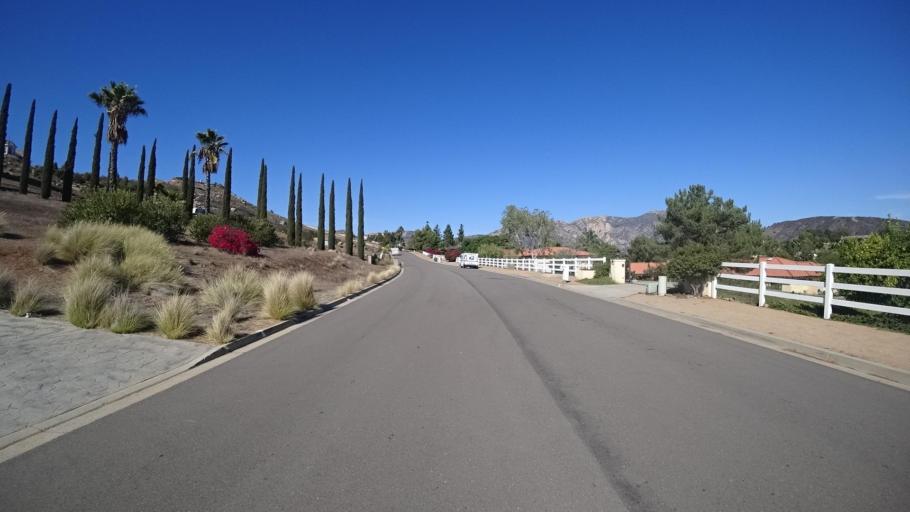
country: US
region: California
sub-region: San Diego County
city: Lakeside
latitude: 32.8688
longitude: -116.8672
